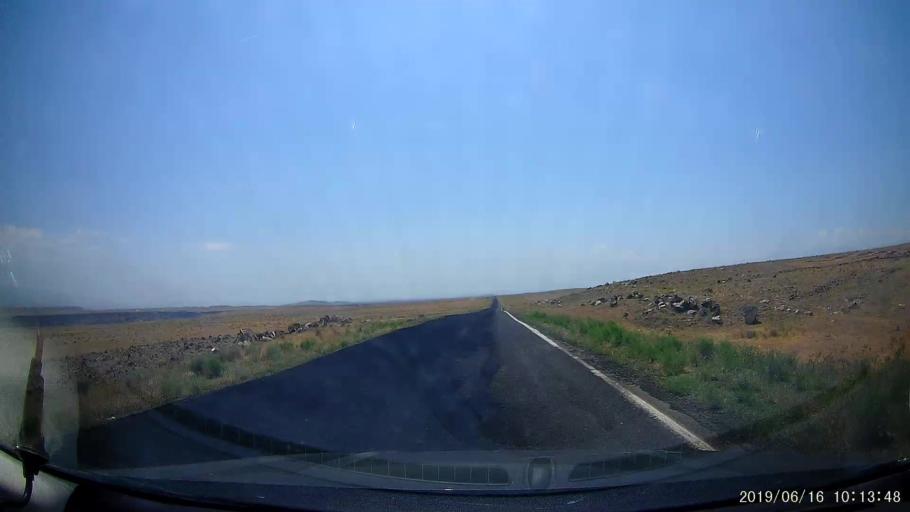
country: TR
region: Igdir
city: Tuzluca
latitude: 40.1903
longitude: 43.6498
